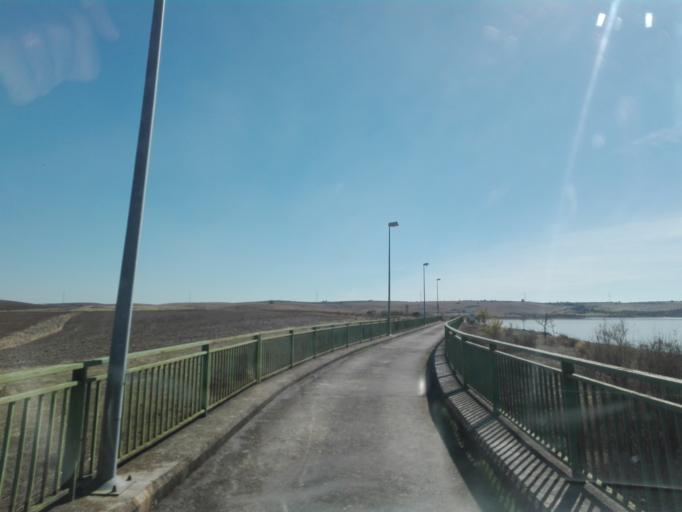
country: ES
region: Extremadura
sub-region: Provincia de Badajoz
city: Ahillones
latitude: 38.3138
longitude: -5.9103
